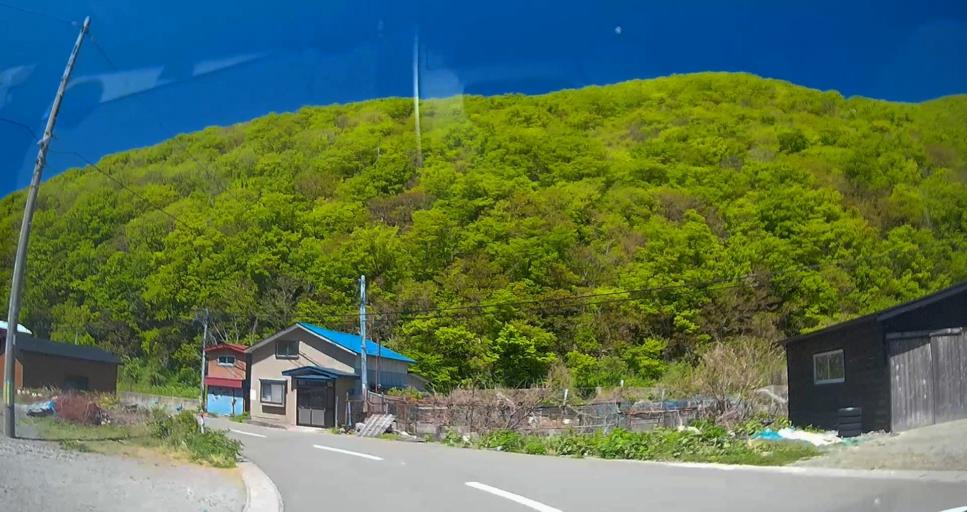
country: JP
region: Aomori
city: Mutsu
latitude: 41.3278
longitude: 140.8117
